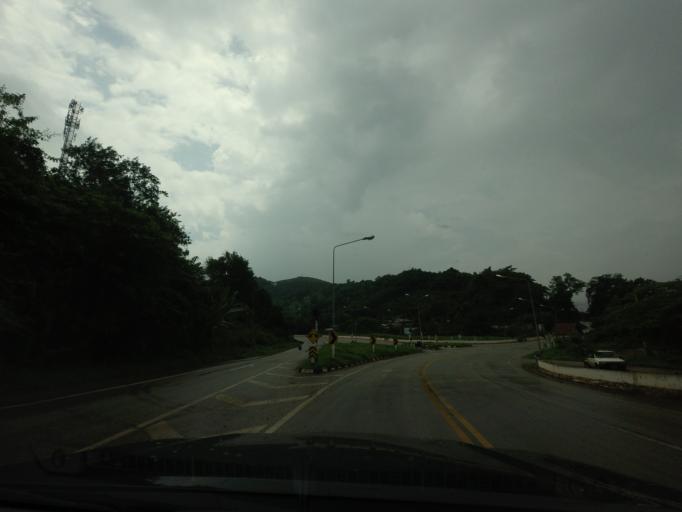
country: TH
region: Loei
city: Pak Chom
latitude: 18.1203
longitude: 101.9976
